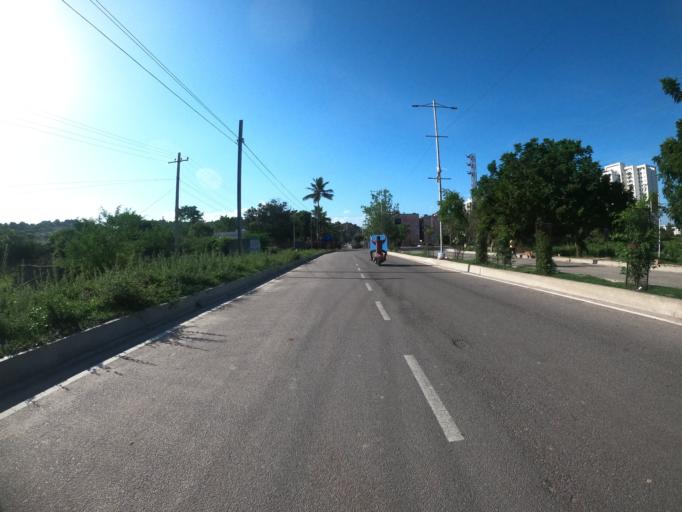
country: IN
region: Telangana
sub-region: Hyderabad
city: Hyderabad
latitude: 17.3563
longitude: 78.3696
